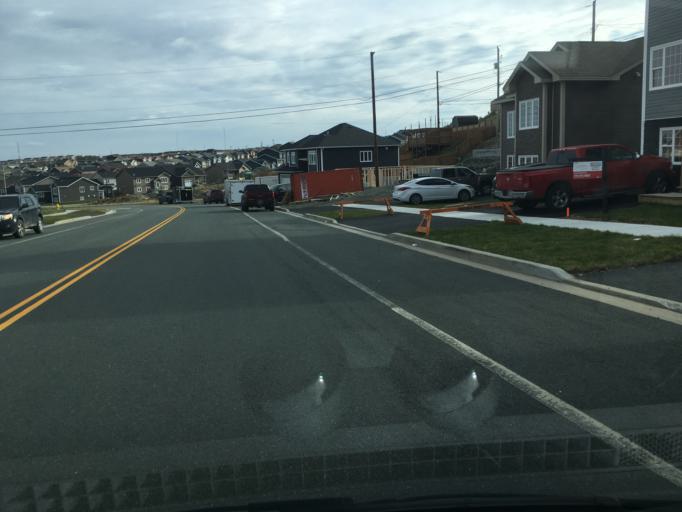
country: CA
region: Newfoundland and Labrador
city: Mount Pearl
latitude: 47.5556
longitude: -52.7991
